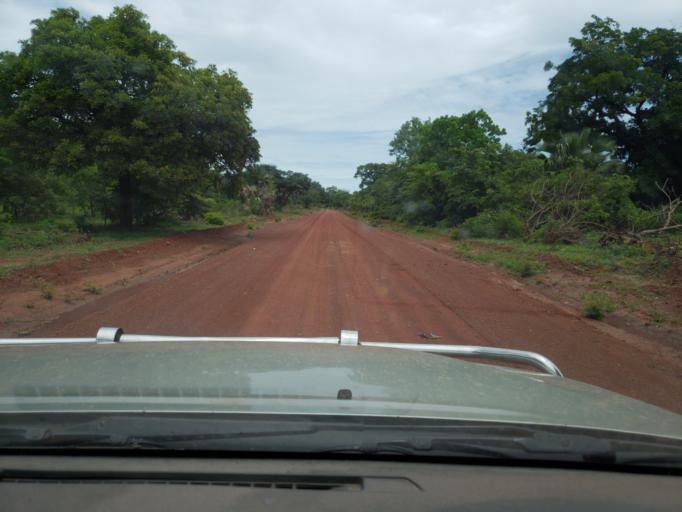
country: ML
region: Sikasso
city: Sikasso
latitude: 11.6602
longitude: -6.3421
